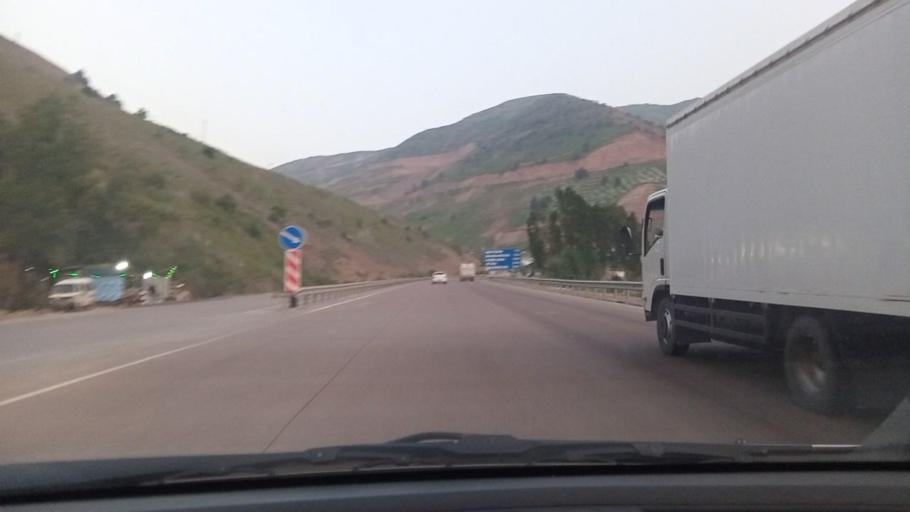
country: UZ
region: Toshkent
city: Angren
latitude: 41.1122
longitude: 70.4976
